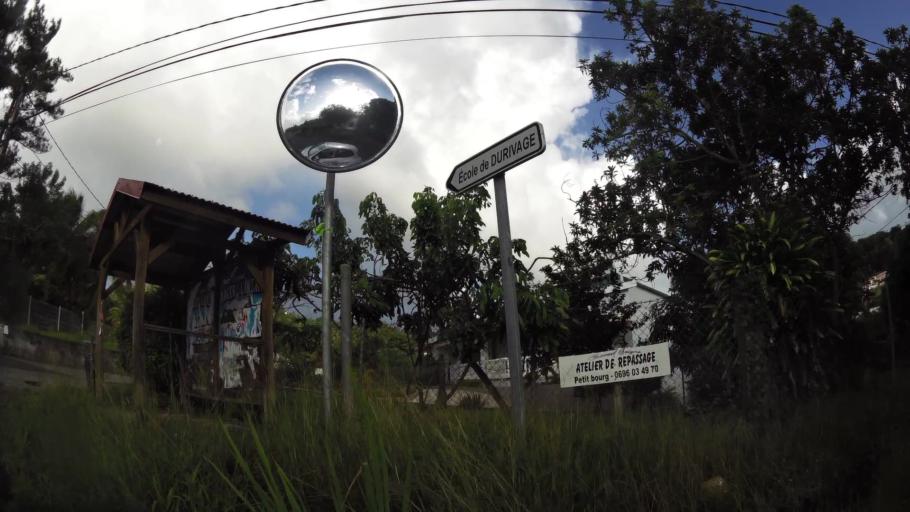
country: MQ
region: Martinique
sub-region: Martinique
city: Ducos
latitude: 14.5599
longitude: -60.9631
